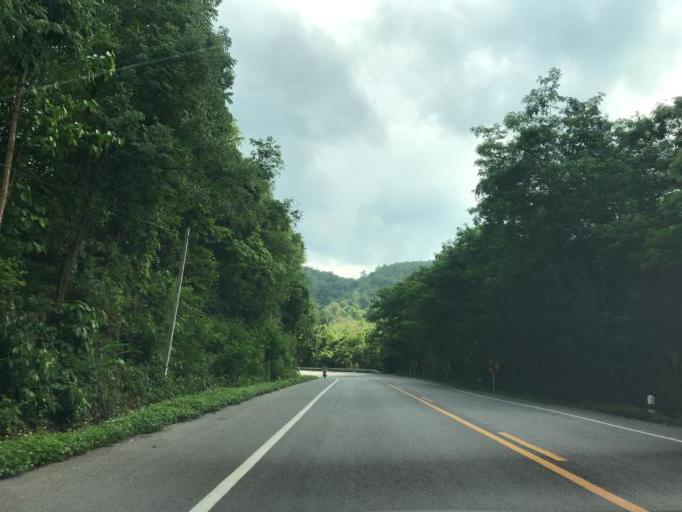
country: TH
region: Phayao
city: Phayao
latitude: 19.0873
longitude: 99.8204
